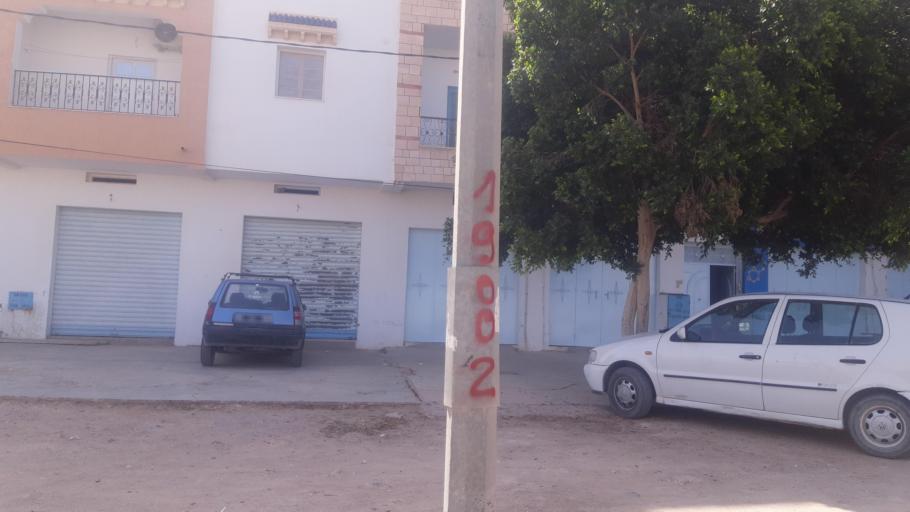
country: TN
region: Madanin
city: Medenine
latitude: 33.3141
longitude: 10.4816
